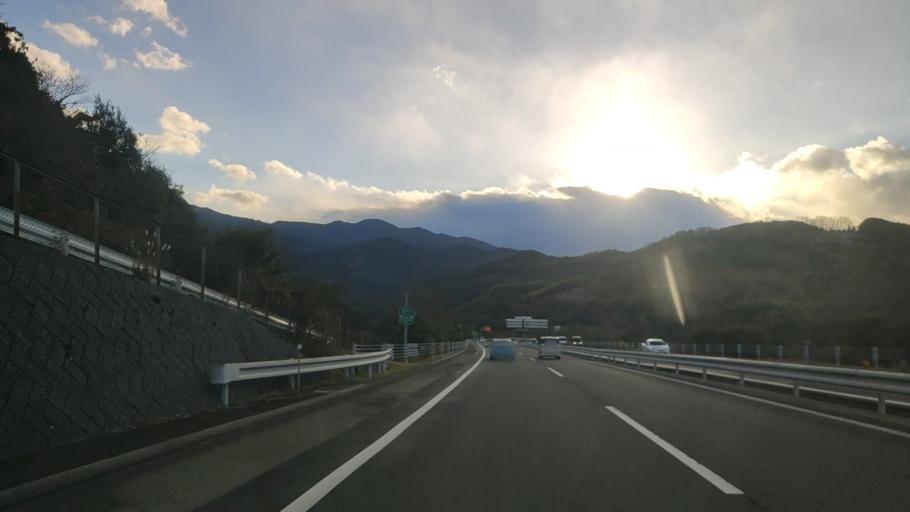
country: JP
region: Ehime
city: Saijo
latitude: 33.8799
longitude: 133.0845
